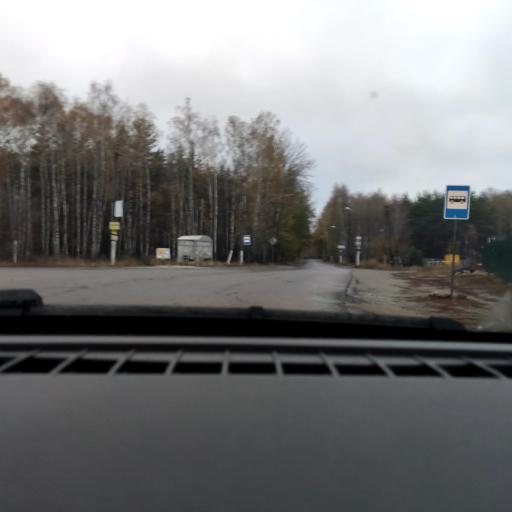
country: RU
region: Voronezj
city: Somovo
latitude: 51.6929
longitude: 39.3171
